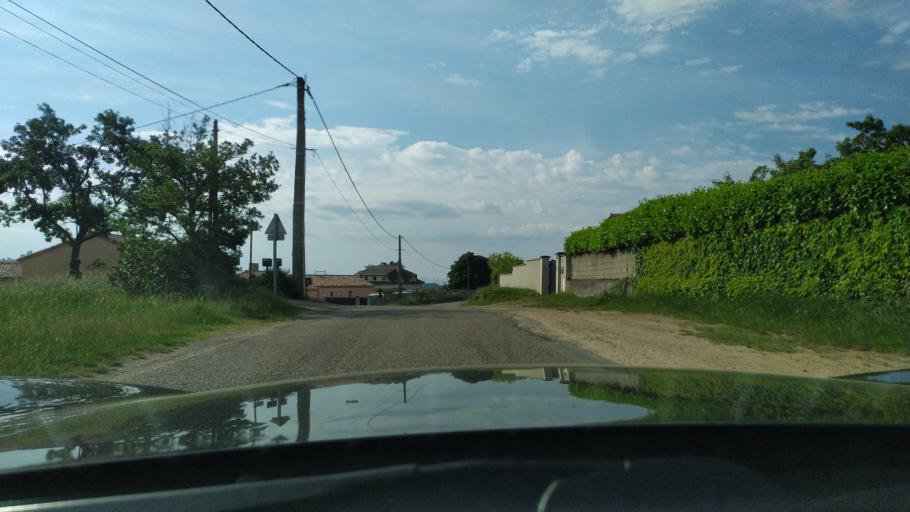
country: FR
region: Rhone-Alpes
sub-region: Departement de l'Ardeche
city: Peaugres
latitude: 45.2973
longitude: 4.7291
